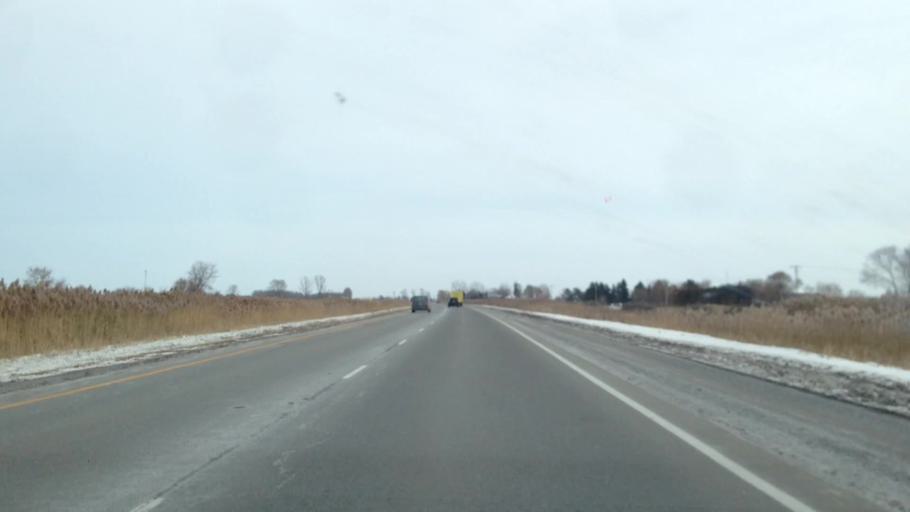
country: CA
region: Ontario
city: Casselman
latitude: 45.3056
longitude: -75.0566
